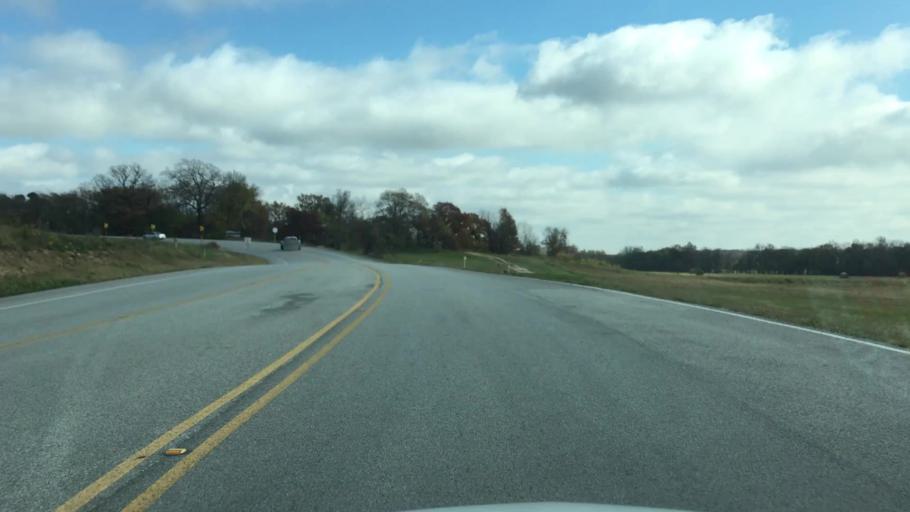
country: US
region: Arkansas
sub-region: Benton County
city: Centerton
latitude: 36.3003
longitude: -94.3061
